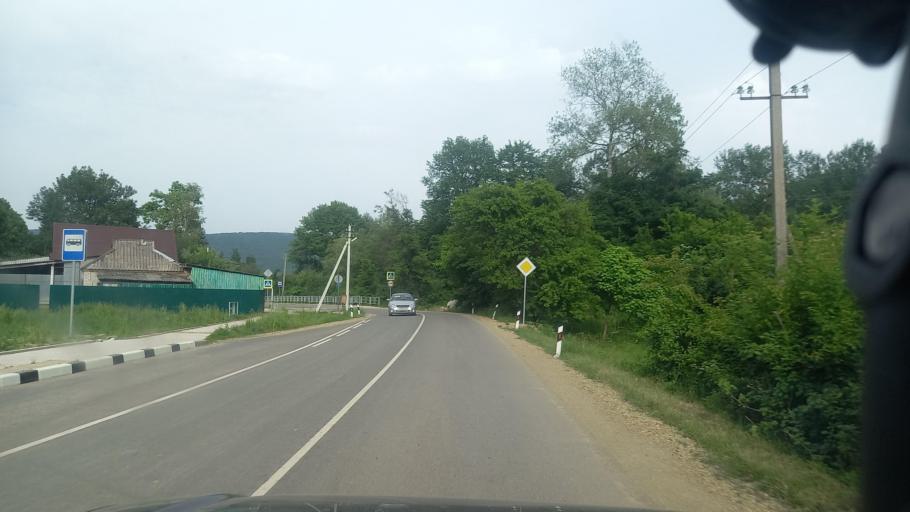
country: RU
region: Krasnodarskiy
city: Goryachiy Klyuch
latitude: 44.6036
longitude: 39.0062
